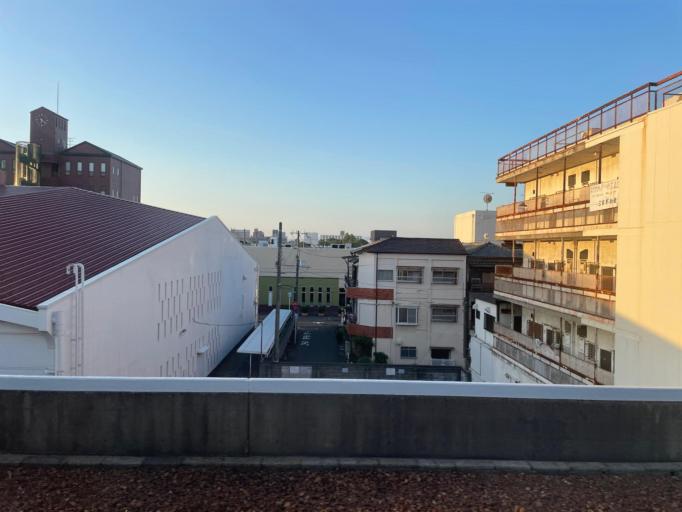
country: JP
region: Osaka
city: Yao
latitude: 34.6638
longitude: 135.5858
